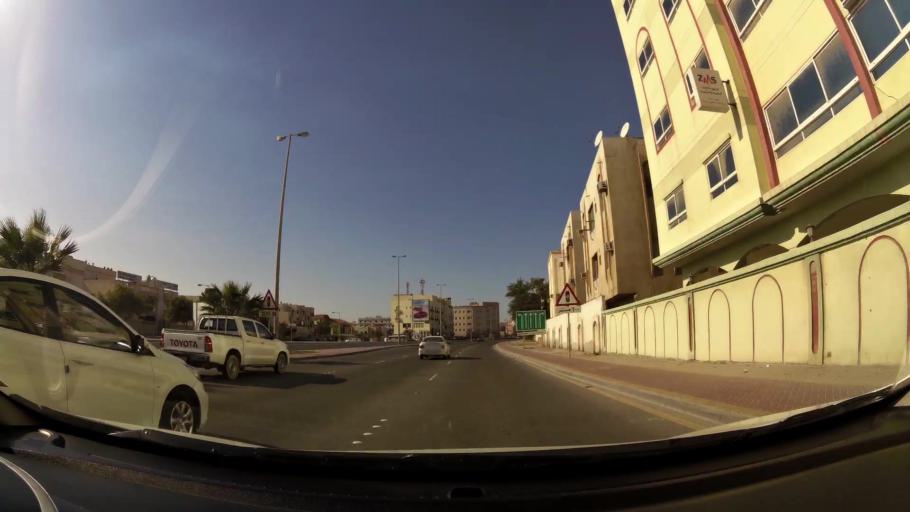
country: BH
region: Manama
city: Manama
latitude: 26.2103
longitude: 50.5665
